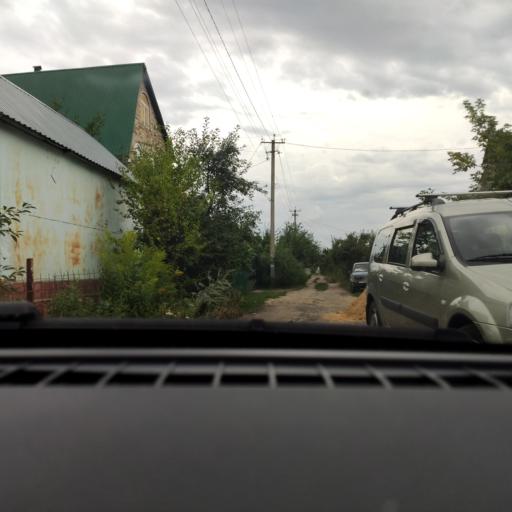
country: RU
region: Voronezj
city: Maslovka
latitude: 51.5207
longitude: 39.2347
